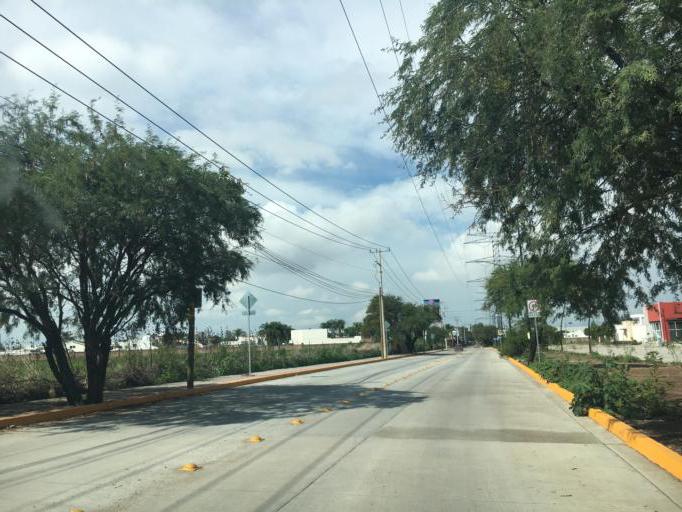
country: MX
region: Guanajuato
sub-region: Leon
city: Medina
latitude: 21.1341
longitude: -101.6235
